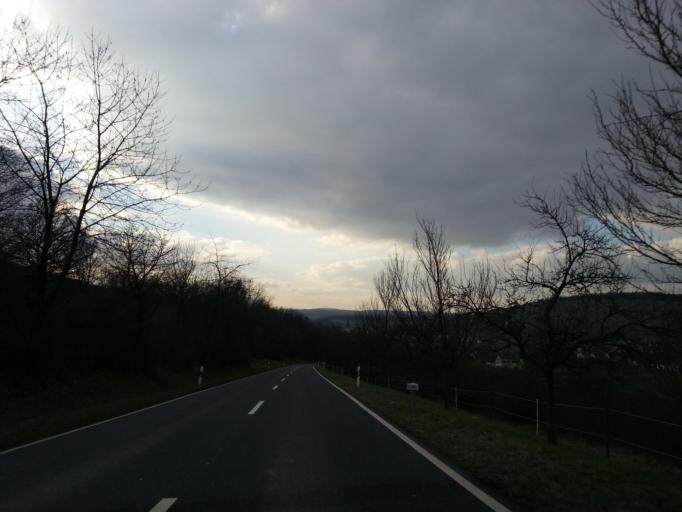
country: DE
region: Bavaria
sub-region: Regierungsbezirk Unterfranken
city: Neubrunn
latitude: 49.7636
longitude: 9.6292
